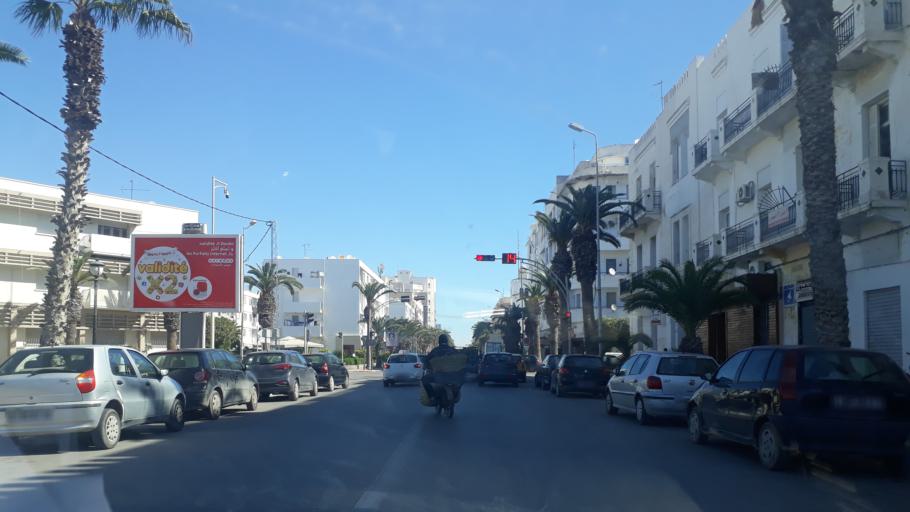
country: TN
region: Safaqis
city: Sfax
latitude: 34.7292
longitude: 10.7596
